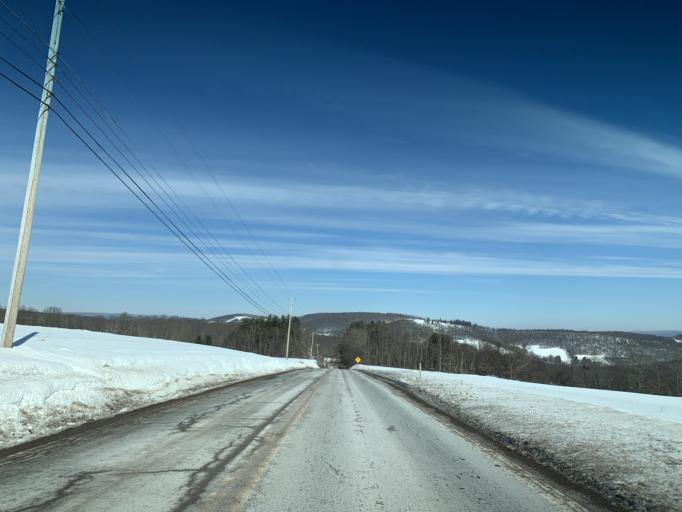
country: US
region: West Virginia
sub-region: Preston County
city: Terra Alta
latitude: 39.6817
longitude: -79.4508
